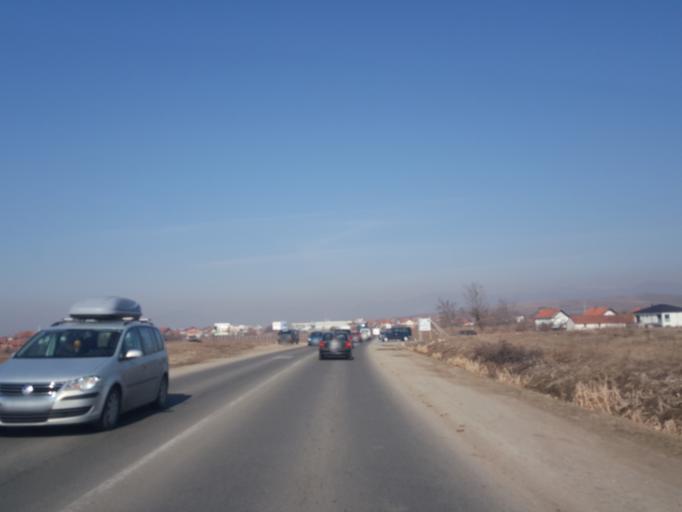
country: XK
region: Mitrovica
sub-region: Vushtrri
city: Vushtrri
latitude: 42.7772
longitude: 21.0147
